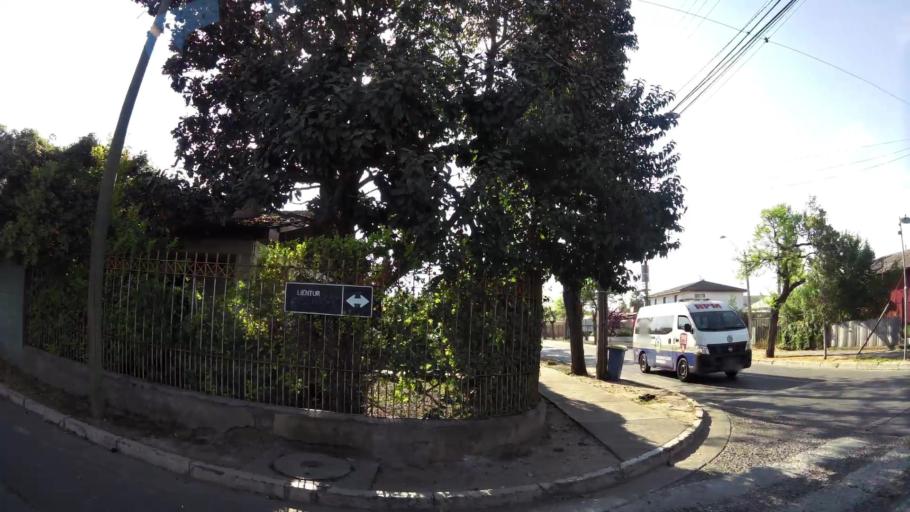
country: CL
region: Santiago Metropolitan
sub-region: Provincia de Santiago
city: La Pintana
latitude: -33.5649
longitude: -70.5923
